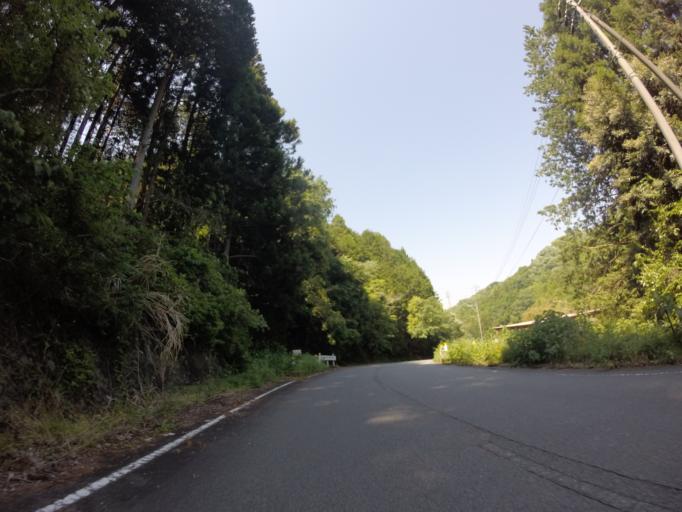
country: JP
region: Shizuoka
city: Fujinomiya
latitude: 35.1621
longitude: 138.5727
